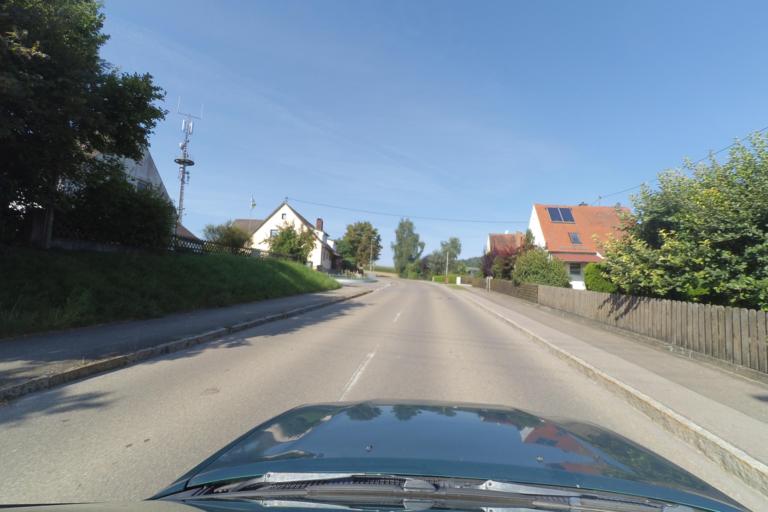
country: DE
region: Bavaria
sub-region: Swabia
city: Marxheim
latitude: 48.7420
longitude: 10.9424
